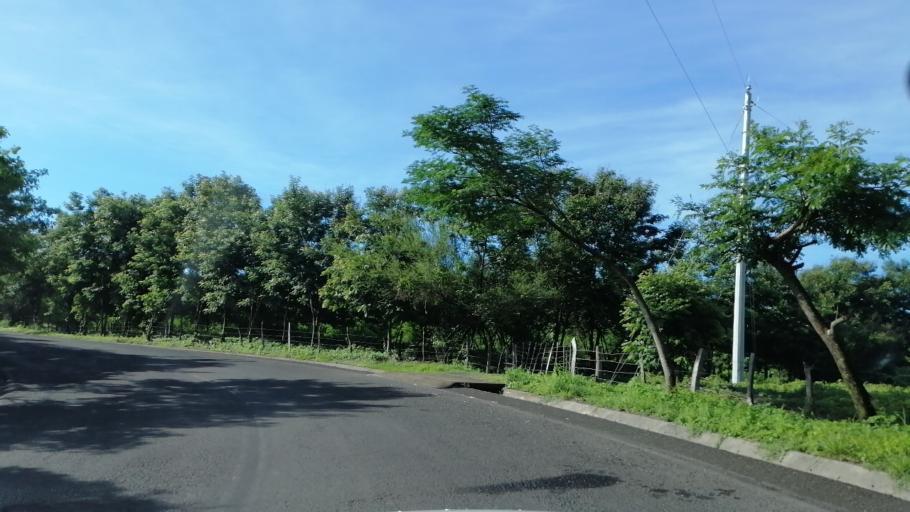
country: SV
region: Morazan
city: Cacaopera
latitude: 13.7855
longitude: -88.1099
